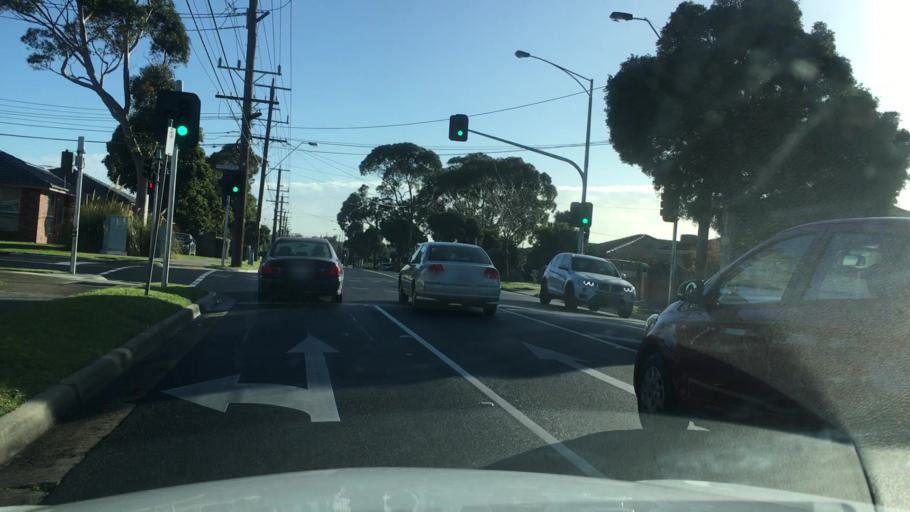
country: AU
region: Victoria
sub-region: Greater Dandenong
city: Keysborough
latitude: -37.9822
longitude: 145.1650
